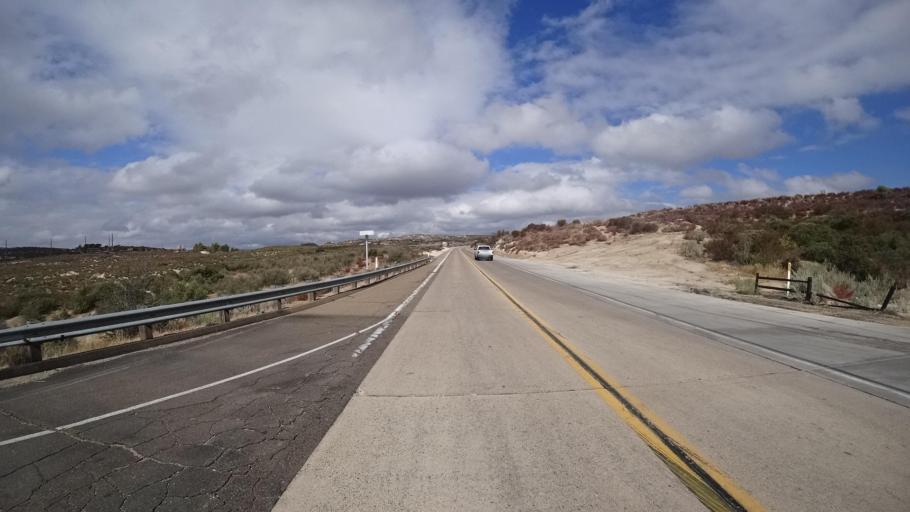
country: US
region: California
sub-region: San Diego County
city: Campo
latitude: 32.7009
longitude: -116.3575
